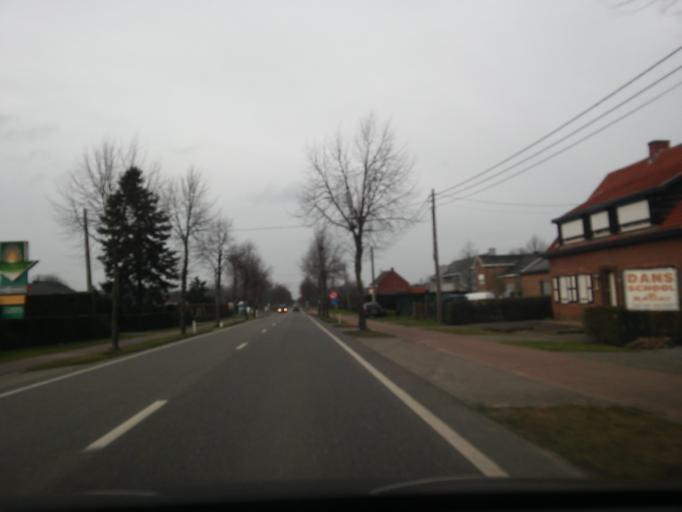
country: BE
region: Flanders
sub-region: Provincie Antwerpen
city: Herselt
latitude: 51.0581
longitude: 4.8838
